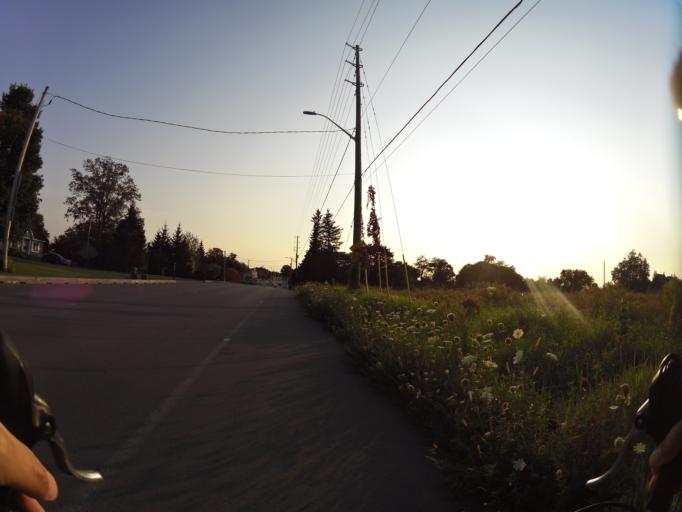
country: CA
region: Ontario
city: Bells Corners
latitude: 45.3568
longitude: -75.9300
